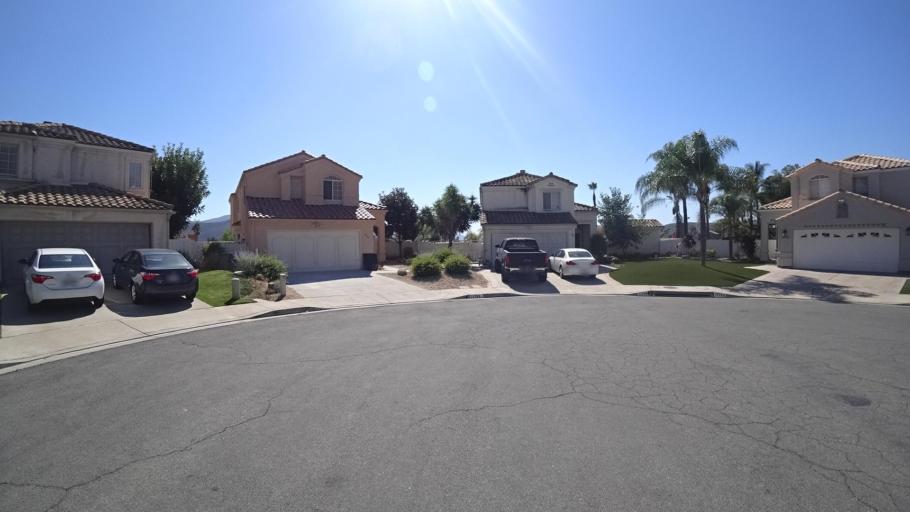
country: US
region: California
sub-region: San Diego County
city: Rancho San Diego
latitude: 32.7508
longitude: -116.9308
